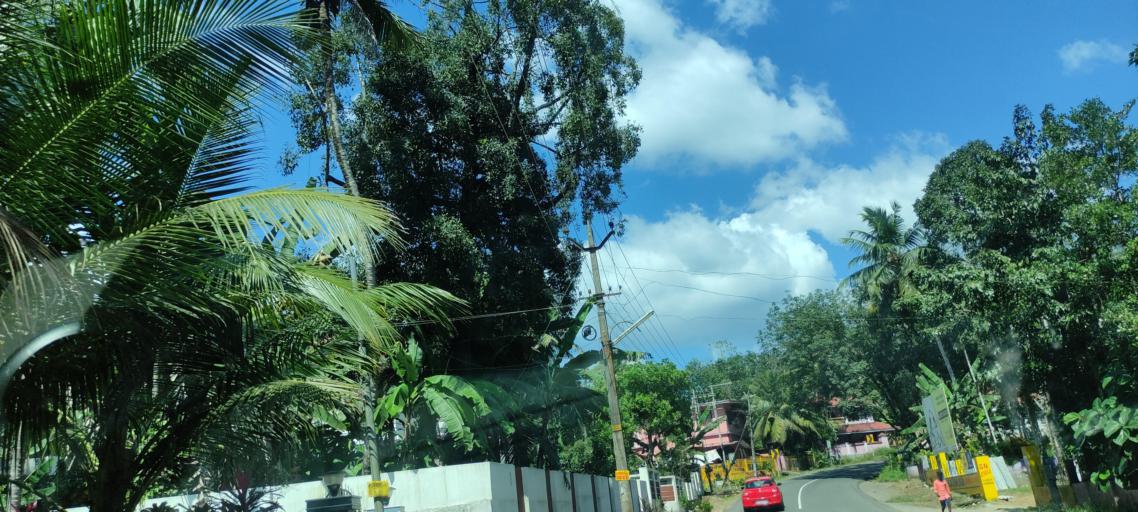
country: IN
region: Kerala
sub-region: Pattanamtitta
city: Adur
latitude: 9.1061
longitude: 76.6902
